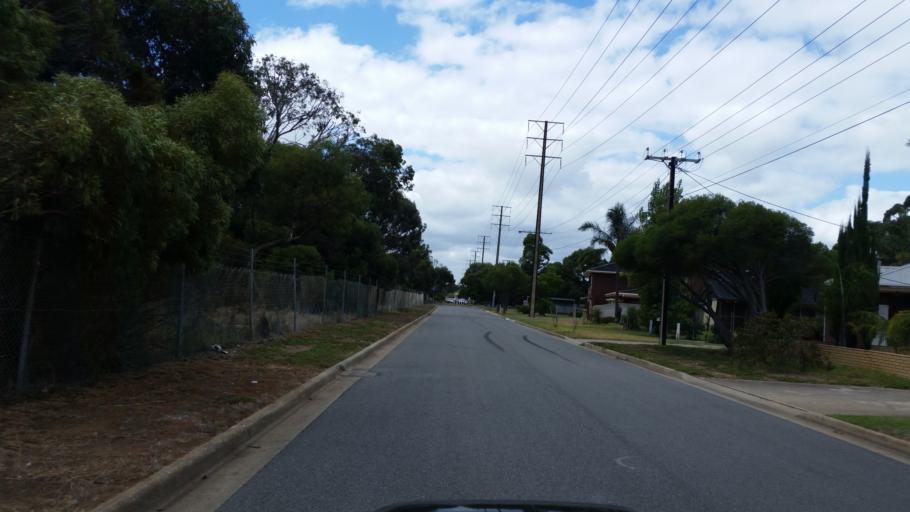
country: AU
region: South Australia
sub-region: Charles Sturt
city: Seaton
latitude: -34.9007
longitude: 138.5098
